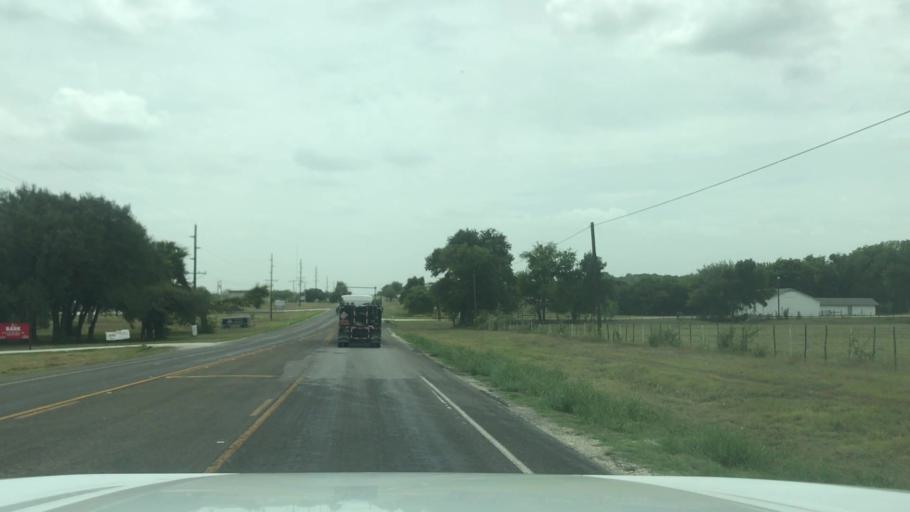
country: US
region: Texas
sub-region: Bosque County
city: Clifton
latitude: 31.7653
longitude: -97.5665
